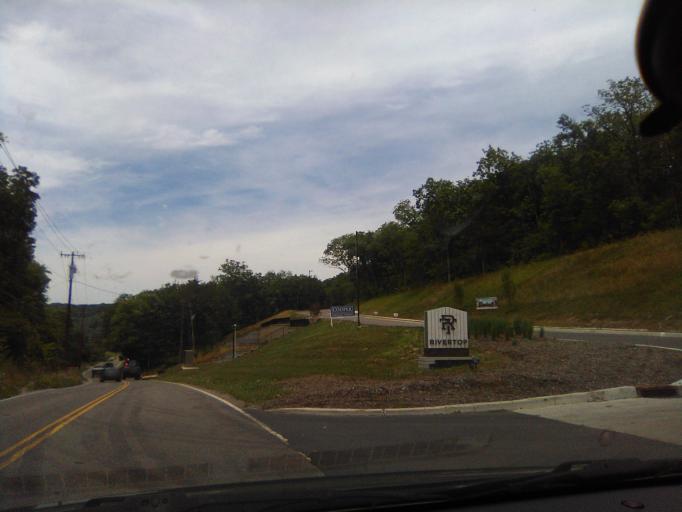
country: US
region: Tennessee
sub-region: Davidson County
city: Belle Meade
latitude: 36.1301
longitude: -86.9129
